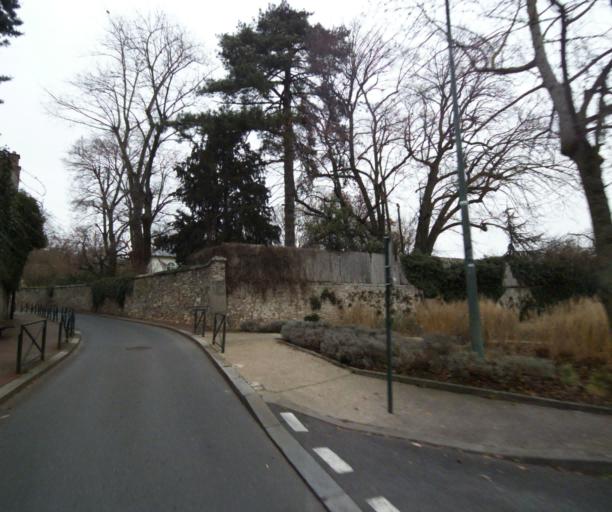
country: FR
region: Ile-de-France
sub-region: Departement des Hauts-de-Seine
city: Vaucresson
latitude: 48.8388
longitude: 2.1594
